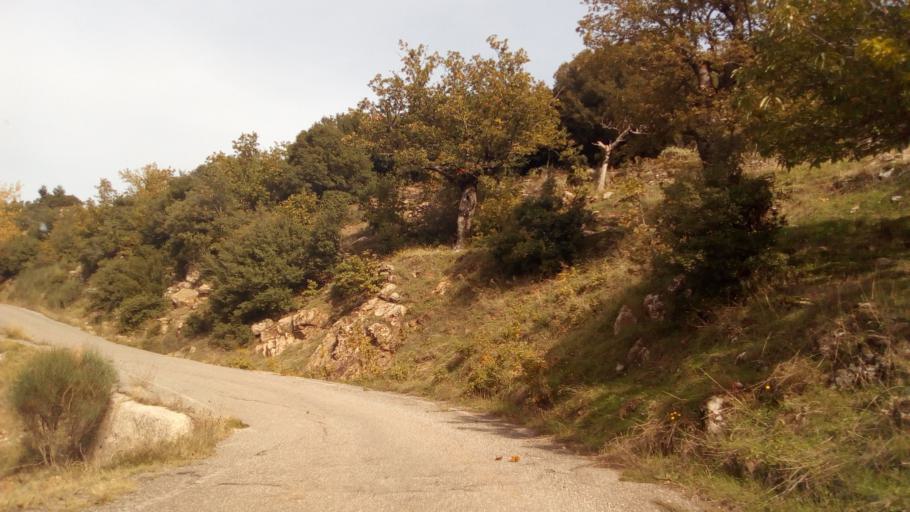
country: GR
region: West Greece
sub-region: Nomos Aitolias kai Akarnanias
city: Thermo
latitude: 38.5556
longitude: 21.8126
